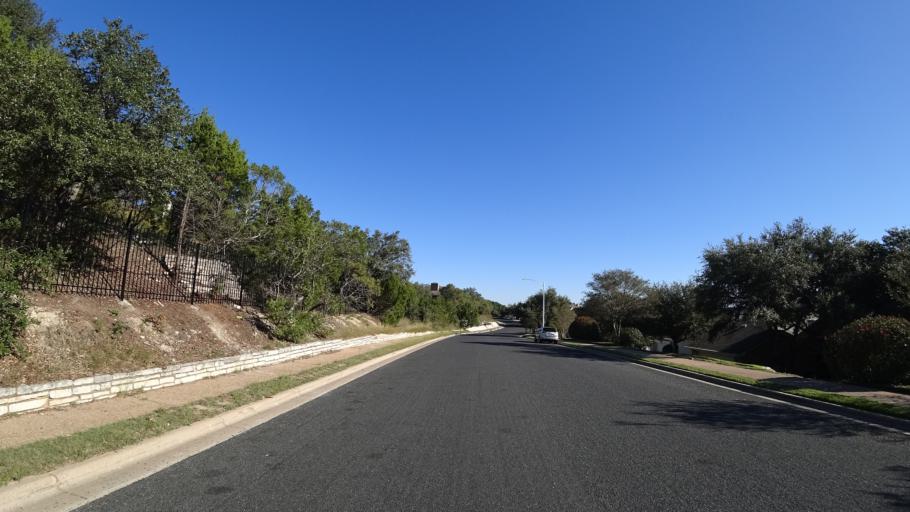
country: US
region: Texas
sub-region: Travis County
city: West Lake Hills
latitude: 30.3355
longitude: -97.8013
